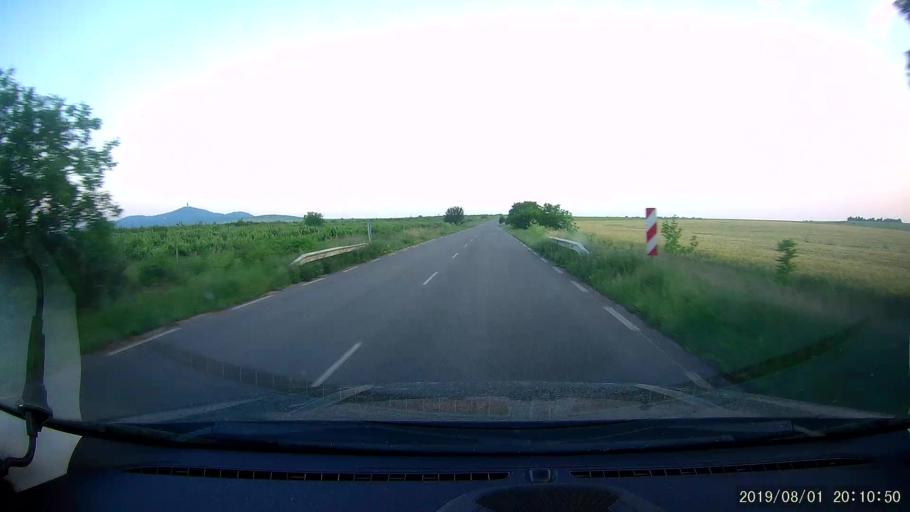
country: BG
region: Yambol
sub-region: Obshtina Yambol
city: Yambol
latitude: 42.4737
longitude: 26.6030
